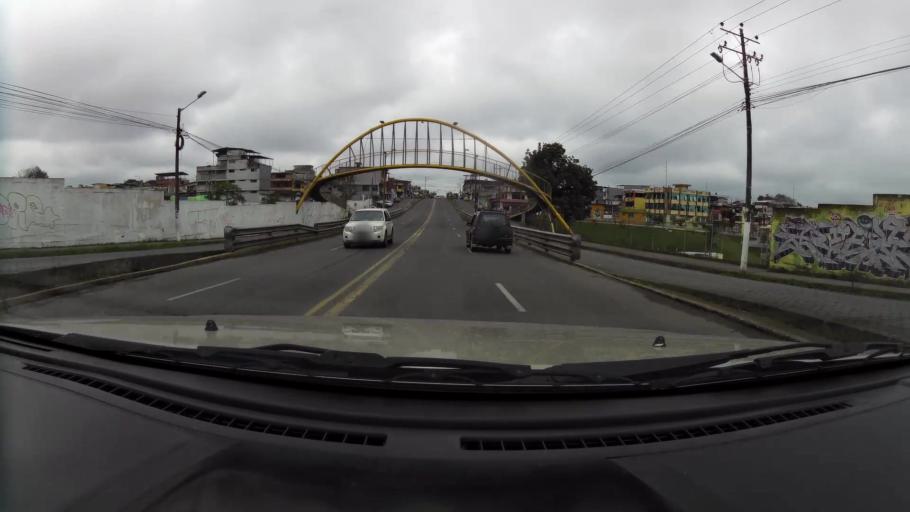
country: EC
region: Santo Domingo de los Tsachilas
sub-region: Canton Santo Domingo de los Colorados
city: Santo Domingo de los Colorados
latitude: -0.2468
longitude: -79.1838
